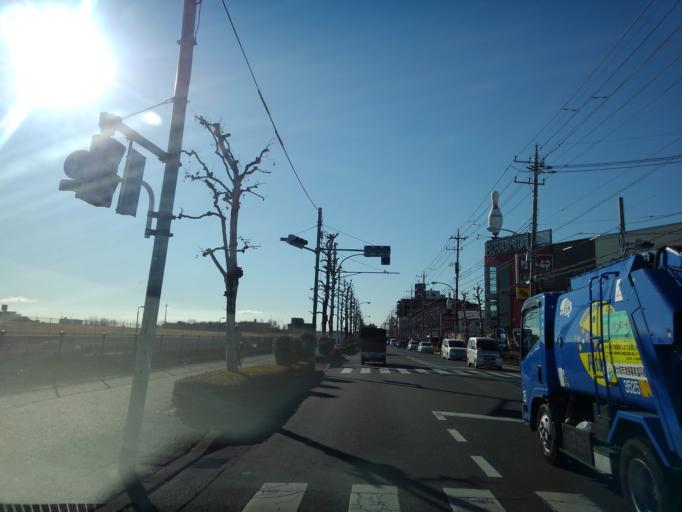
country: JP
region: Tokyo
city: Fussa
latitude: 35.7362
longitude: 139.3830
